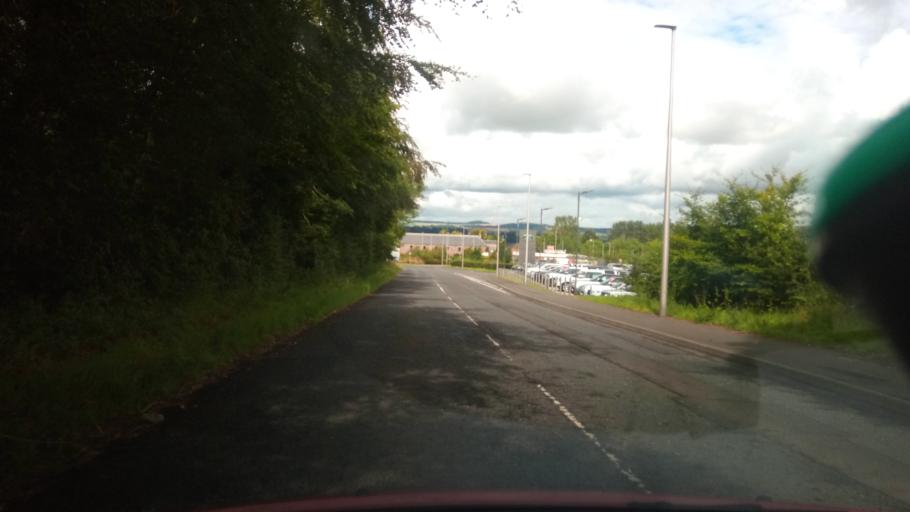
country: GB
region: Scotland
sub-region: The Scottish Borders
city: Kelso
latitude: 55.5885
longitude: -2.4268
